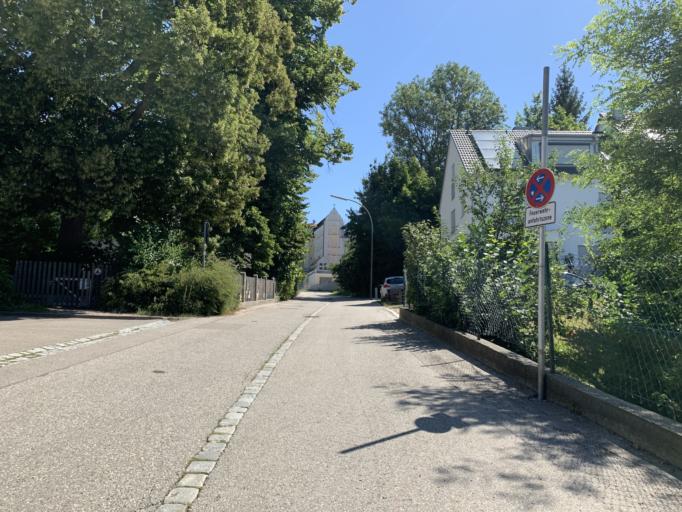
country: DE
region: Bavaria
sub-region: Upper Bavaria
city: Freising
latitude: 48.3958
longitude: 11.7231
